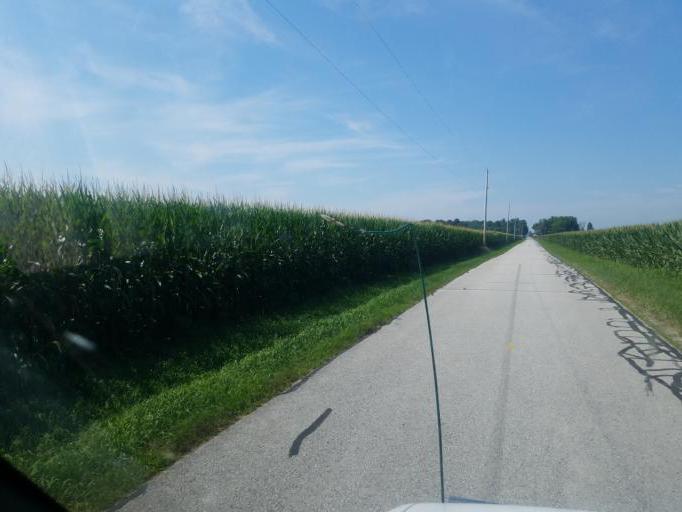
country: US
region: Ohio
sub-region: Shelby County
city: Jackson Center
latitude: 40.5150
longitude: -84.0120
